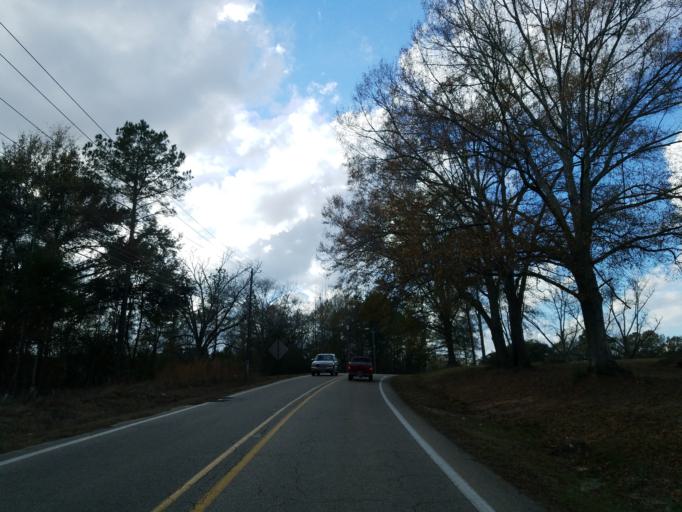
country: US
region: Mississippi
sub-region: Jones County
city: Ellisville
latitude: 31.5940
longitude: -89.1912
